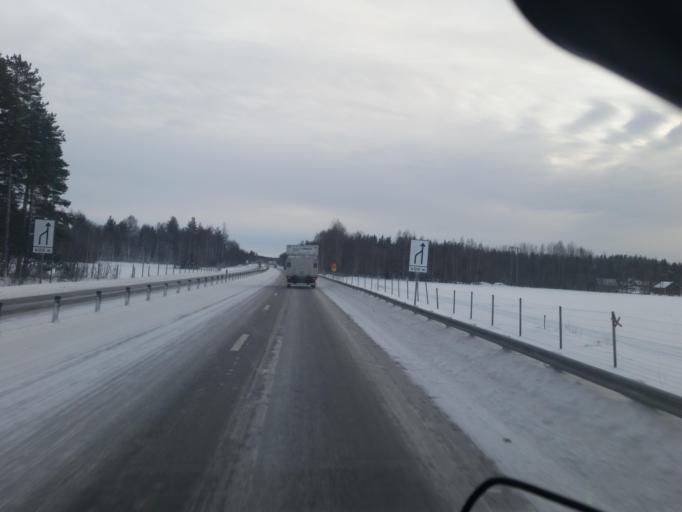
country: SE
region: Norrbotten
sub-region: Pitea Kommun
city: Bergsviken
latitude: 65.2978
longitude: 21.4191
